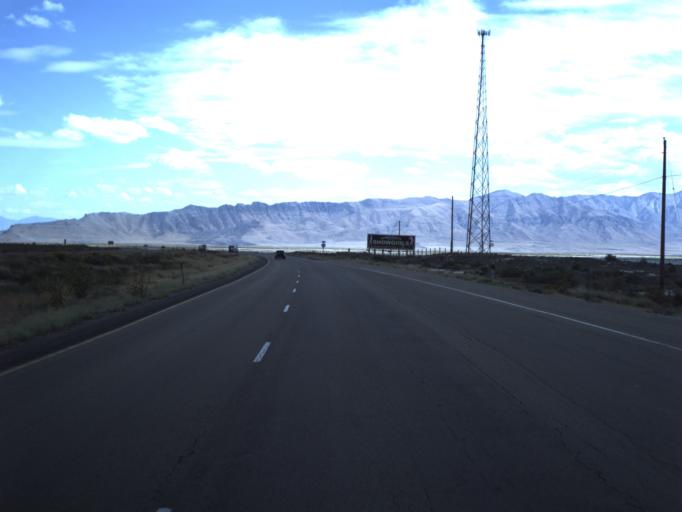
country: US
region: Utah
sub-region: Tooele County
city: Grantsville
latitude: 40.7596
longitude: -112.7757
